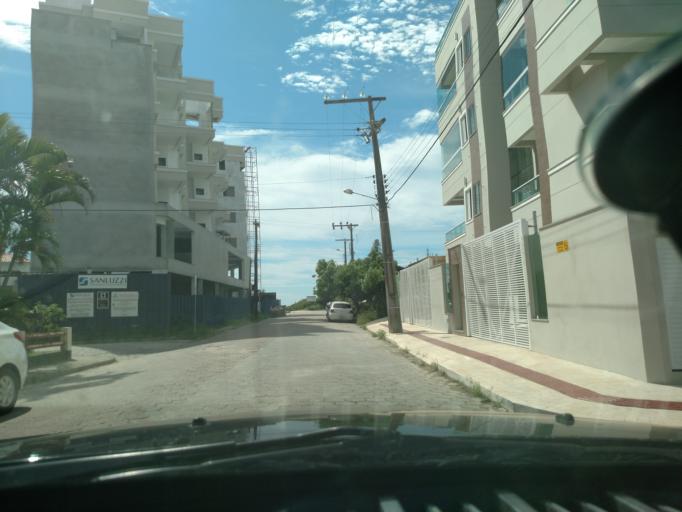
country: BR
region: Santa Catarina
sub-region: Tijucas
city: Tijucas
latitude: -27.3222
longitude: -48.5406
